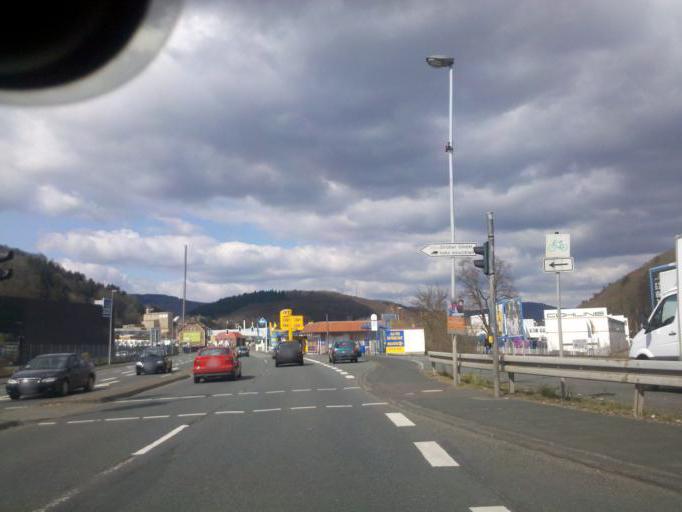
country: DE
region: Hesse
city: Dillenburg
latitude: 50.7482
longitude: 8.2769
